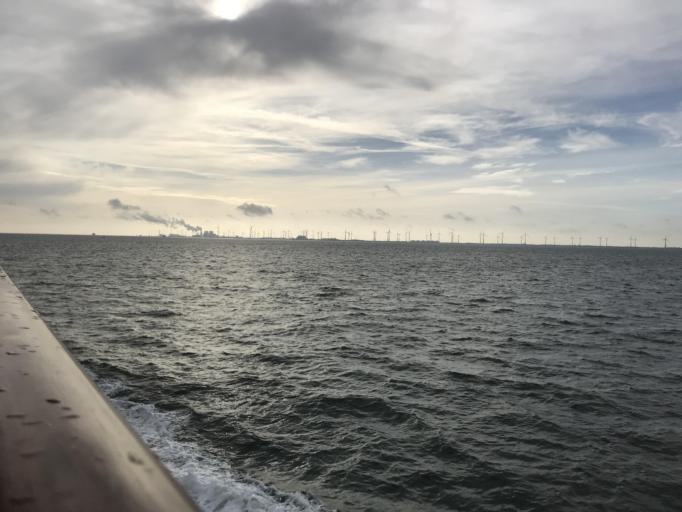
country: DE
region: Lower Saxony
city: Borkum
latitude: 53.5166
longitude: 6.7859
